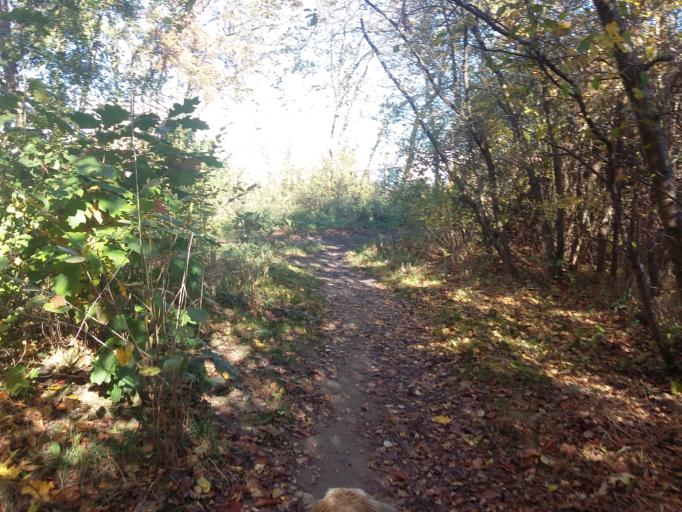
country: PL
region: Lodz Voivodeship
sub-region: Powiat pabianicki
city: Ksawerow
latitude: 51.7393
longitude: 19.4052
